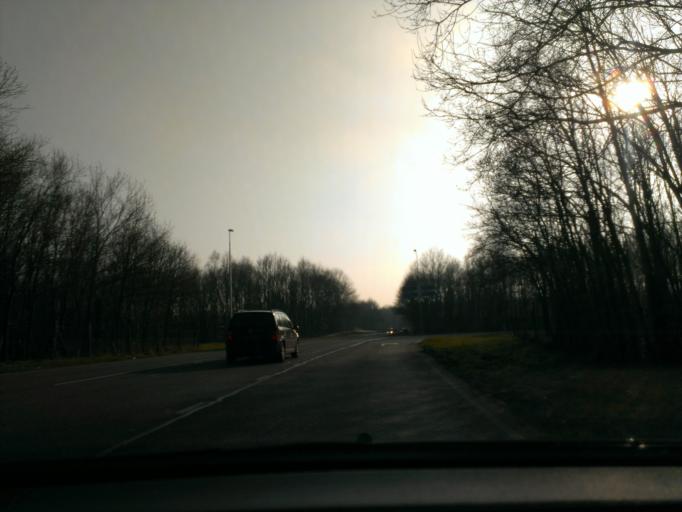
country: NL
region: Overijssel
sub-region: Gemeente Borne
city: Borne
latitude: 52.2939
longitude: 6.7310
